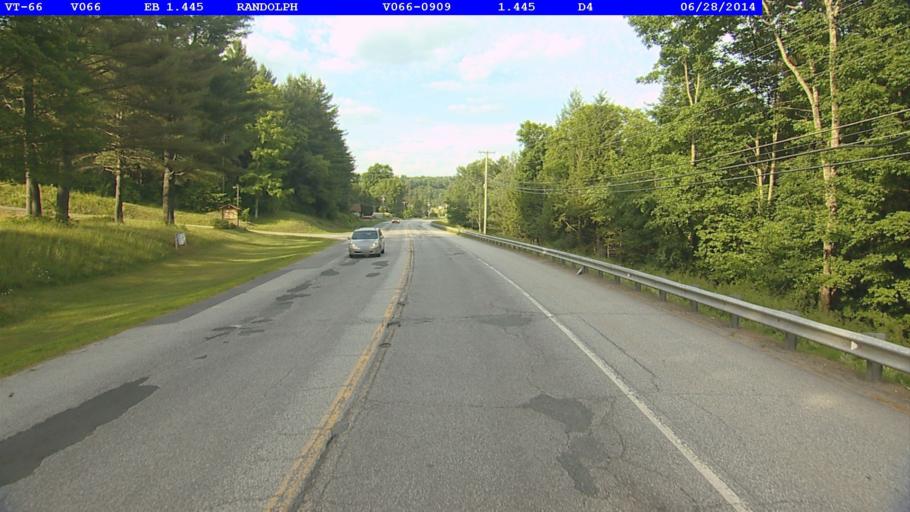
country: US
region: Vermont
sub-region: Orange County
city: Randolph
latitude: 43.9361
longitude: -72.6394
